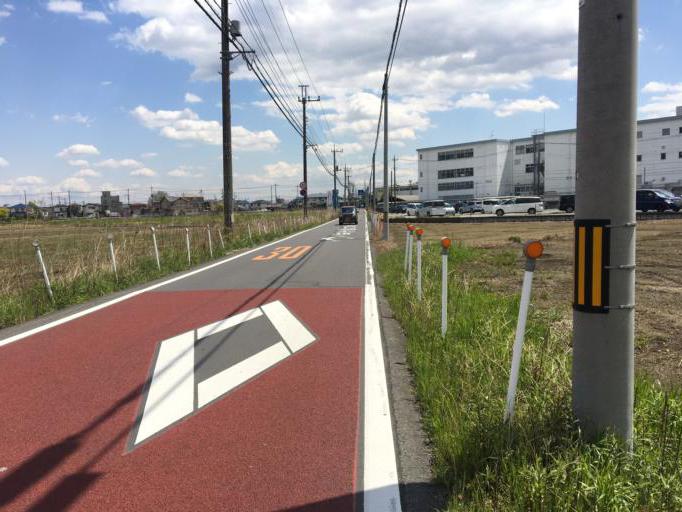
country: JP
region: Saitama
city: Kawagoe
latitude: 35.9341
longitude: 139.4718
